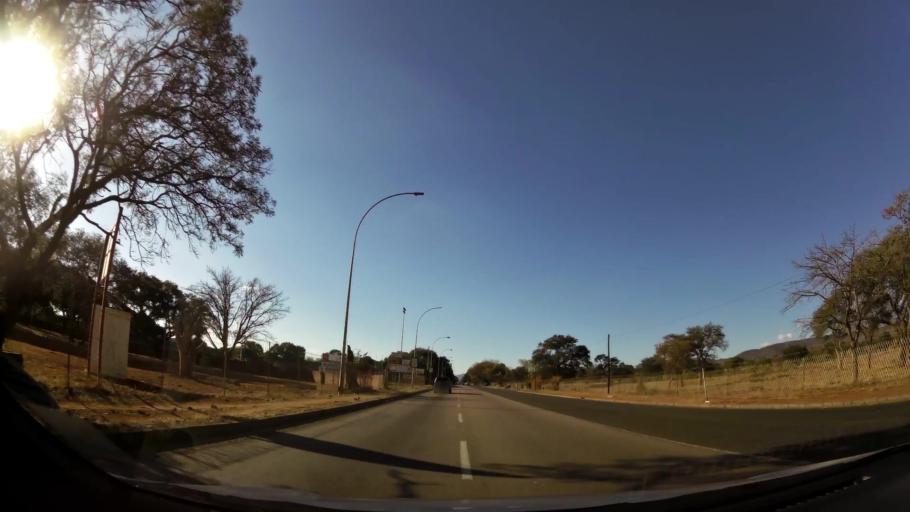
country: ZA
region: Limpopo
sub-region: Waterberg District Municipality
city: Mokopane
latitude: -24.1977
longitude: 29.0077
